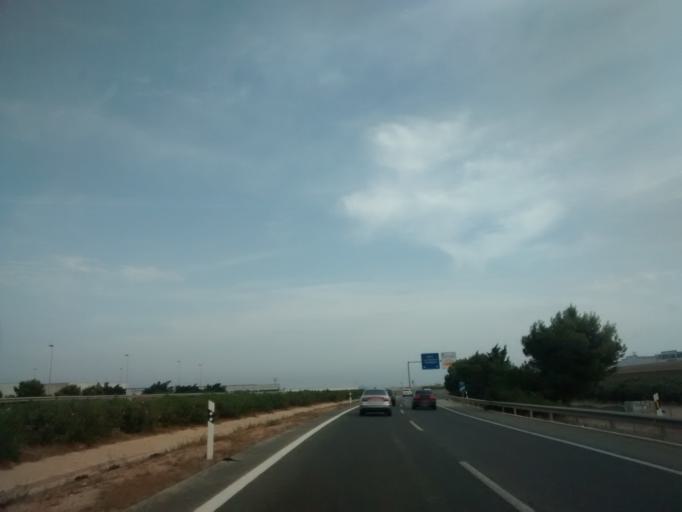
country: ES
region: Murcia
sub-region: Murcia
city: San Javier
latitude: 37.7952
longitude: -0.8403
